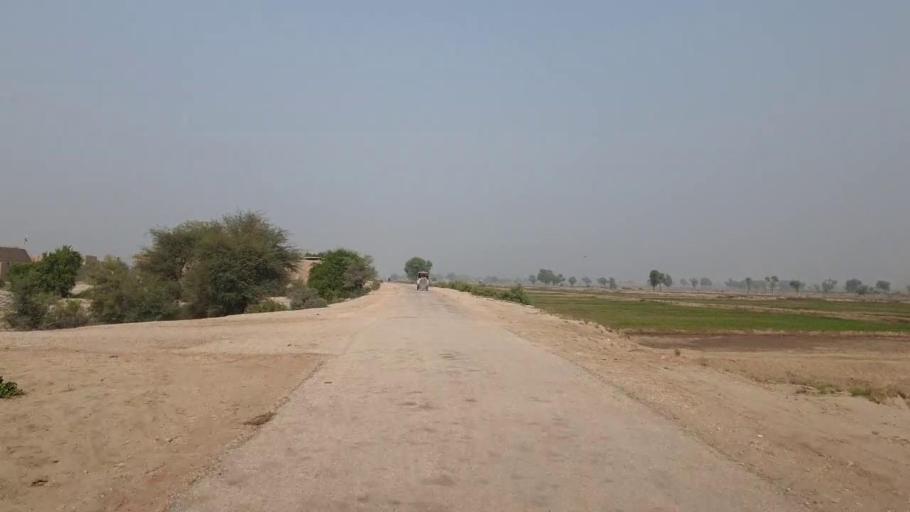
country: PK
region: Sindh
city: Bhan
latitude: 26.5138
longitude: 67.6896
